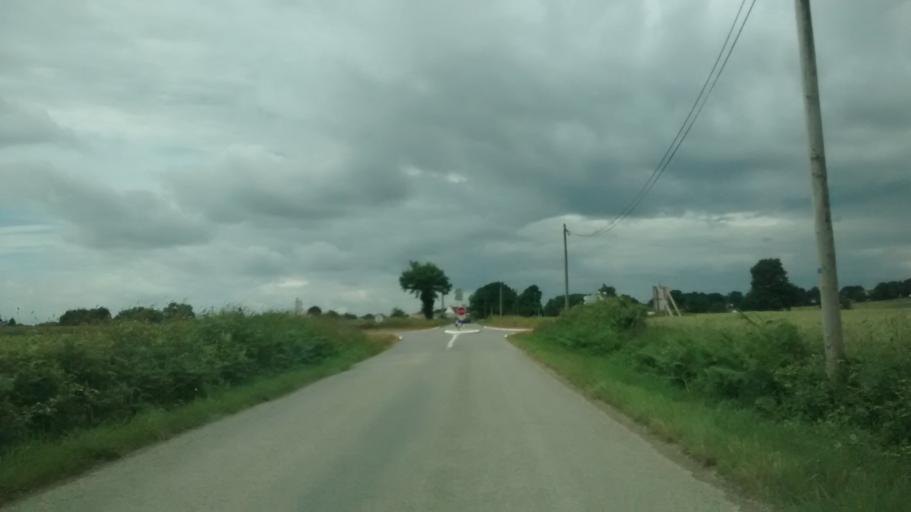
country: FR
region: Brittany
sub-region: Departement du Morbihan
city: Carentoir
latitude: 47.8089
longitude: -2.1241
